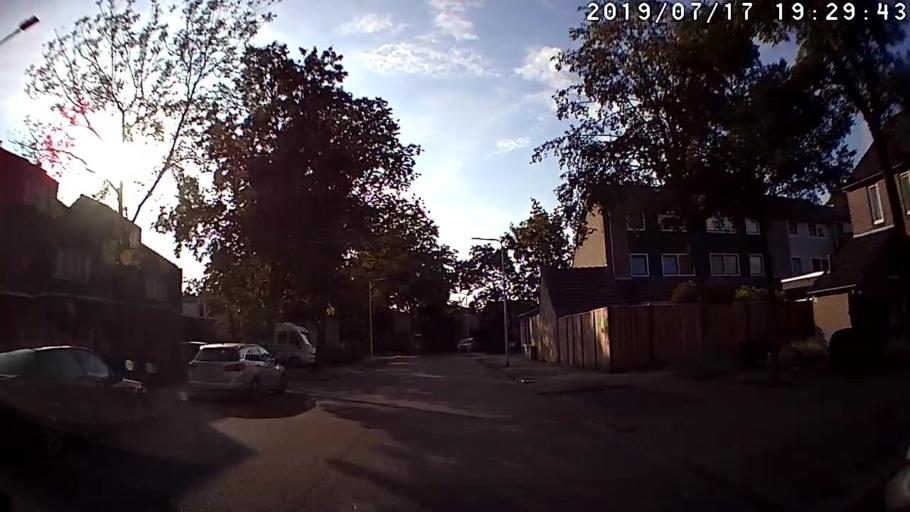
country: NL
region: Overijssel
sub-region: Gemeente Zwolle
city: Zwolle
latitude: 52.5386
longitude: 6.1084
